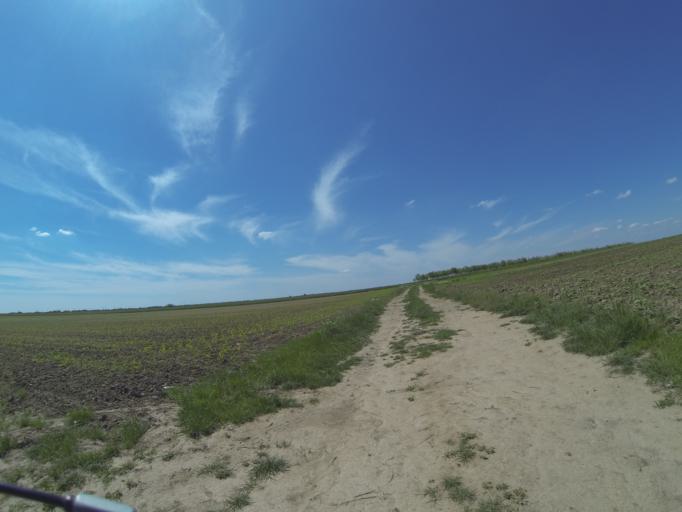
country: RO
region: Dolj
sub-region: Comuna Leu
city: Leu
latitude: 44.2198
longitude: 24.0103
